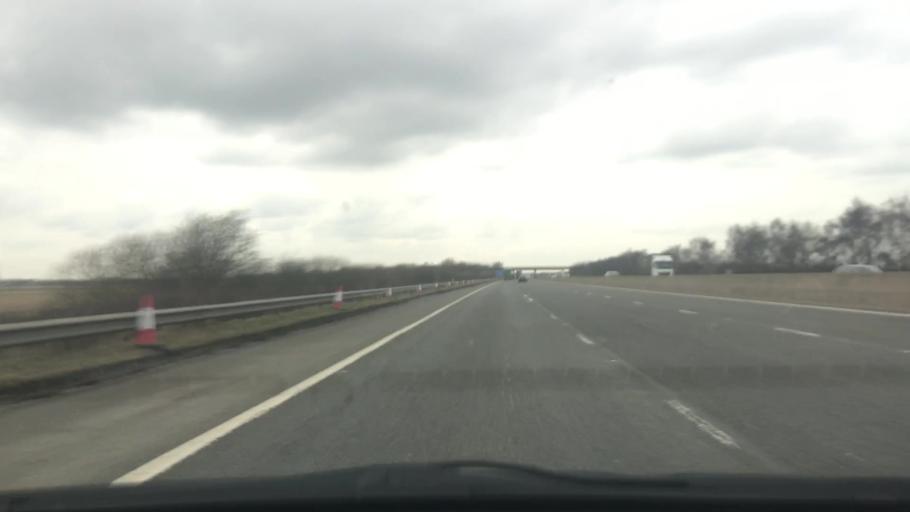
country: GB
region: England
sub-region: Doncaster
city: Hatfield
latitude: 53.5744
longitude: -0.9143
